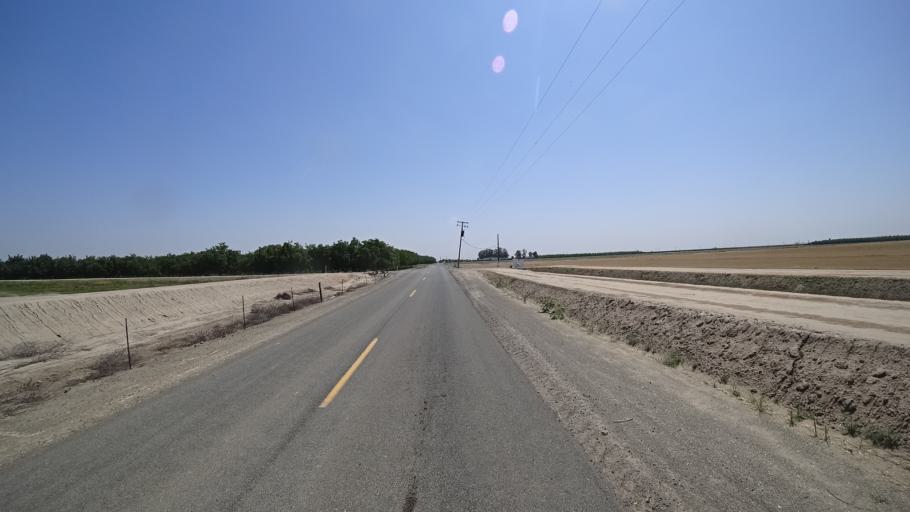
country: US
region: California
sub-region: Kings County
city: Home Garden
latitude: 36.2840
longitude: -119.5724
